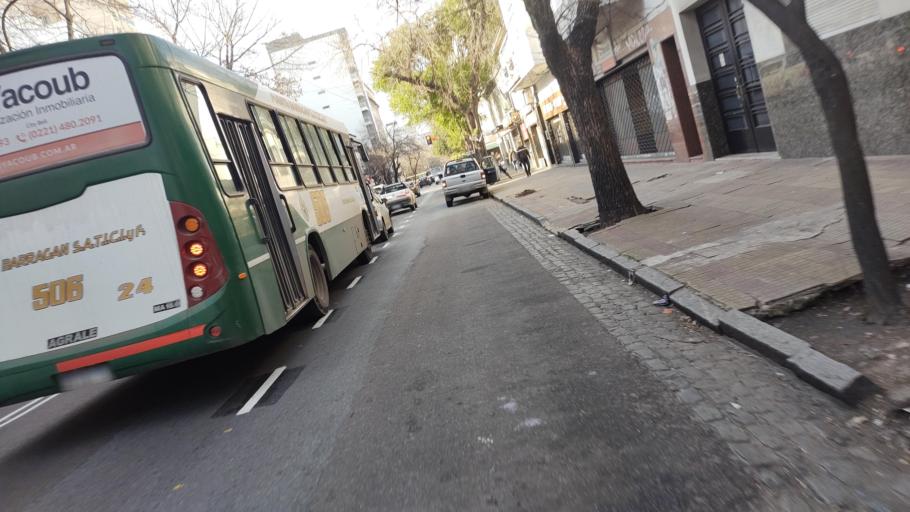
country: AR
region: Buenos Aires
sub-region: Partido de La Plata
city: La Plata
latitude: -34.9182
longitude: -57.9487
